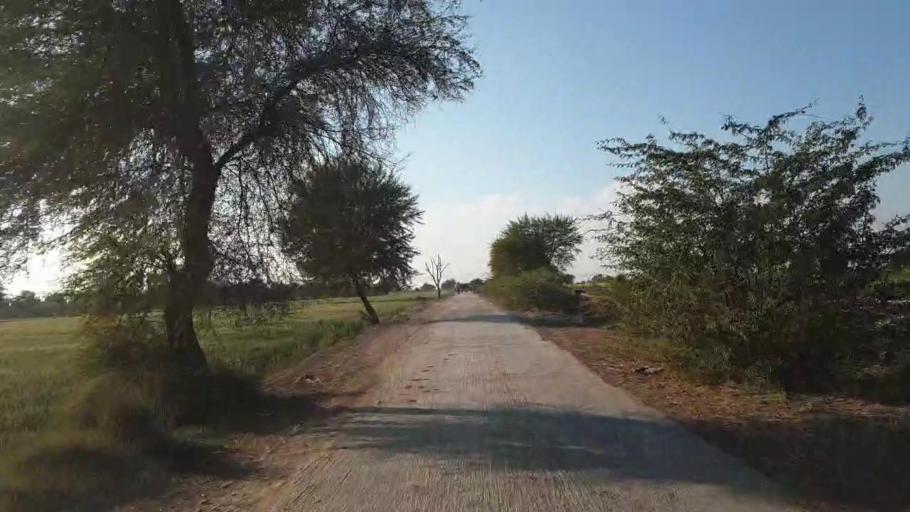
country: PK
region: Sindh
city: Shahpur Chakar
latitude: 26.1357
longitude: 68.5612
